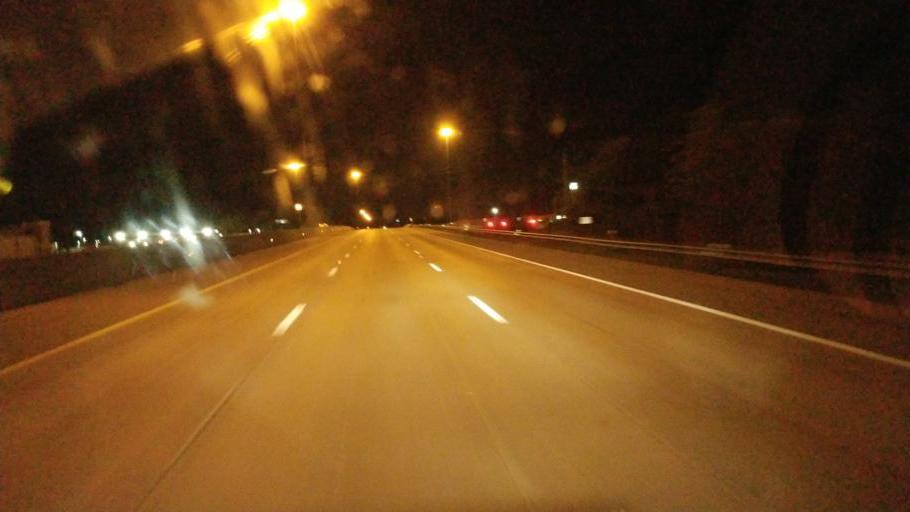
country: US
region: Ohio
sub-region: Montgomery County
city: Huber Heights
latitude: 39.8677
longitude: -84.0973
